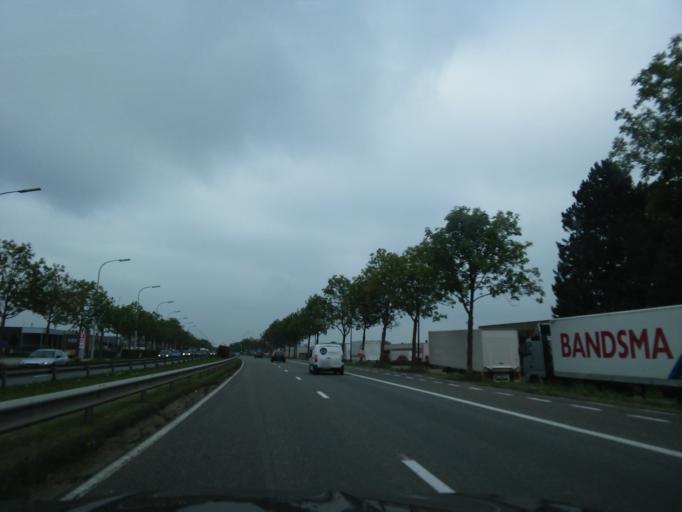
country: BE
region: Flanders
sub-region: Provincie Oost-Vlaanderen
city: Zele
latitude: 51.0732
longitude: 4.0491
